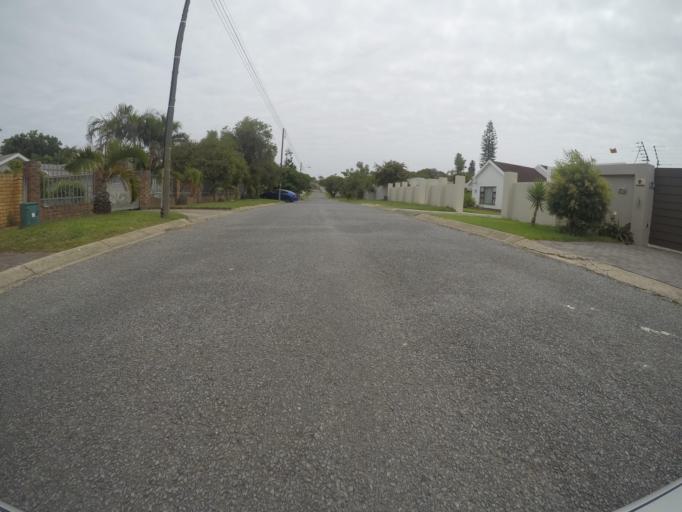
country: ZA
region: Eastern Cape
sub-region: Buffalo City Metropolitan Municipality
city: East London
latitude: -32.9775
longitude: 27.9497
